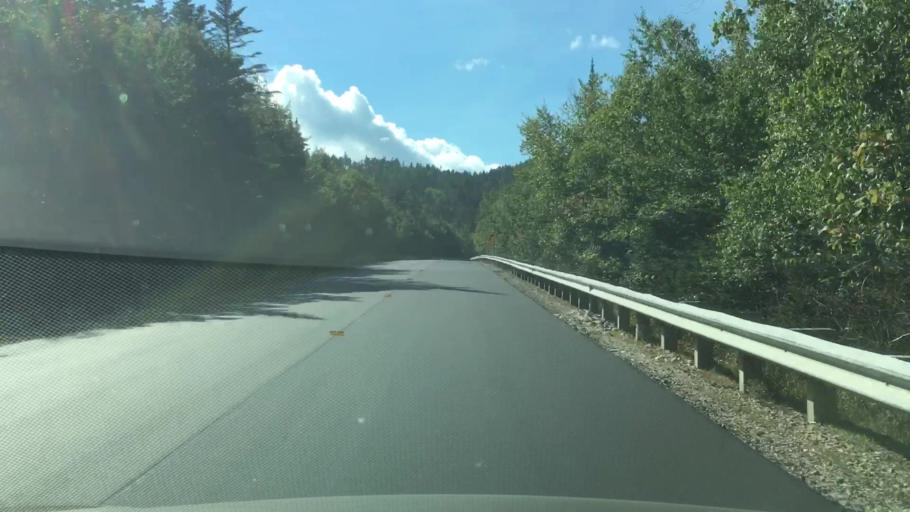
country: US
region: New Hampshire
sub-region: Grafton County
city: Woodstock
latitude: 44.0209
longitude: -71.4882
